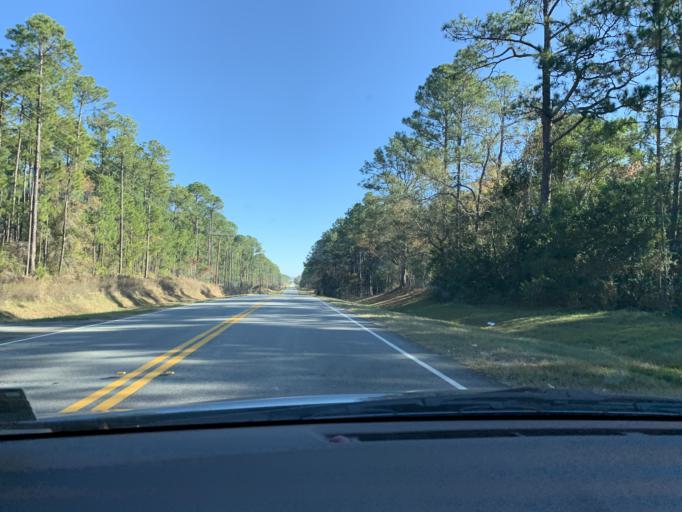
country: US
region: Georgia
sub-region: Ben Hill County
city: Fitzgerald
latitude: 31.7303
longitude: -83.1745
